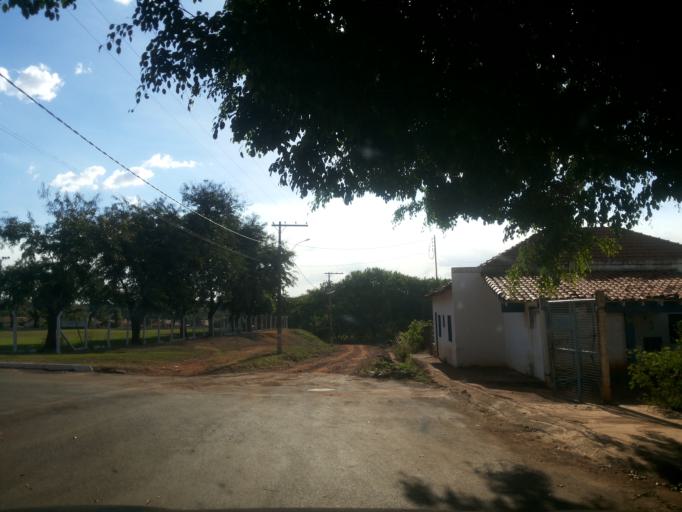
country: BR
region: Minas Gerais
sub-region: Capinopolis
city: Capinopolis
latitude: -18.6828
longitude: -49.5774
